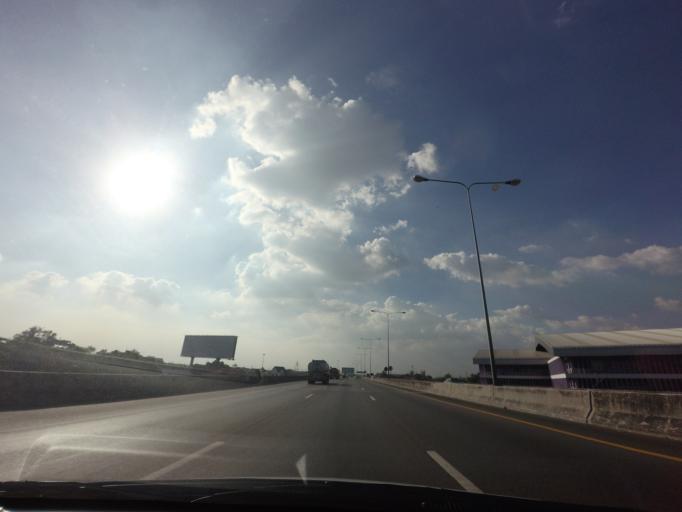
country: TH
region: Samut Prakan
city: Phra Samut Chedi
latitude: 13.6322
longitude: 100.5766
